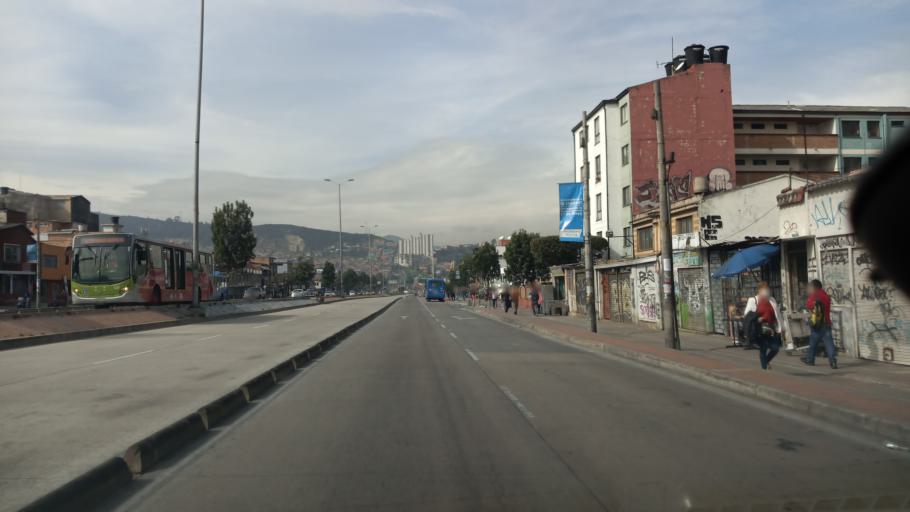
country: CO
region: Bogota D.C.
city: Bogota
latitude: 4.5751
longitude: -74.0954
